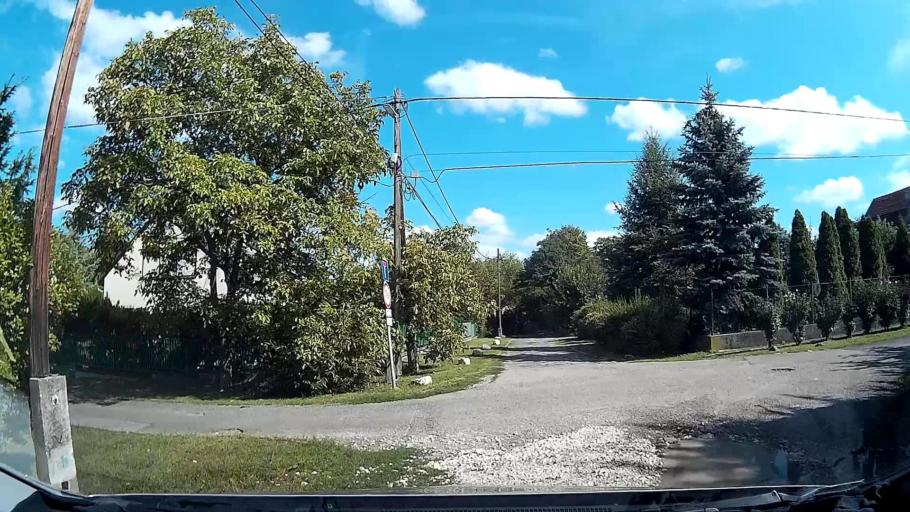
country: HU
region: Pest
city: Szentendre
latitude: 47.6754
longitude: 19.0768
